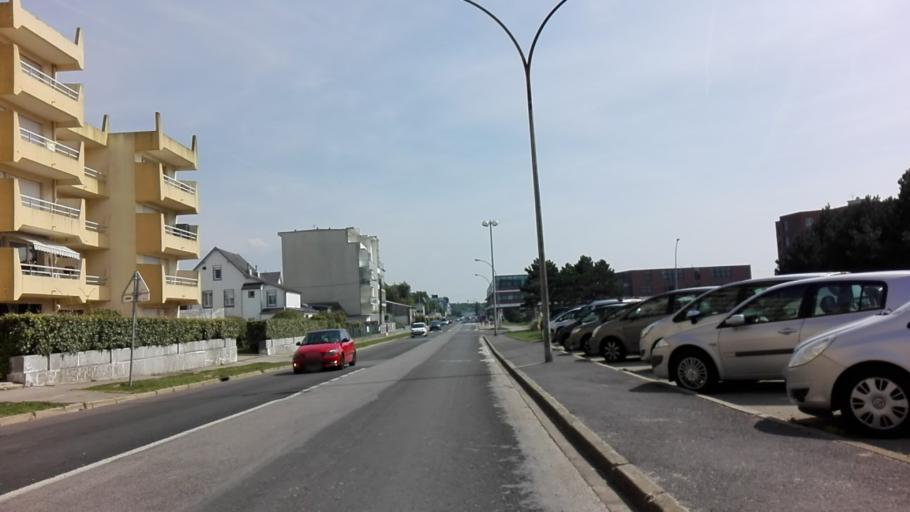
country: FR
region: Nord-Pas-de-Calais
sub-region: Departement du Pas-de-Calais
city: Berck-Plage
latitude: 50.4016
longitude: 1.5609
